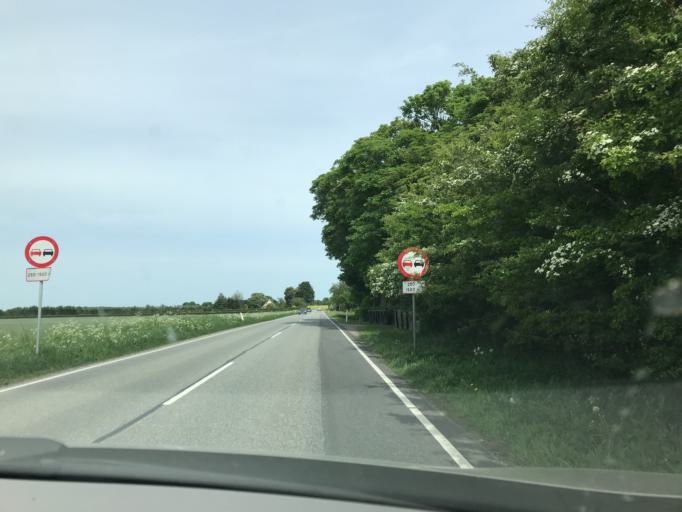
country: DK
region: Central Jutland
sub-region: Norddjurs Kommune
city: Allingabro
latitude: 56.4509
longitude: 10.2900
